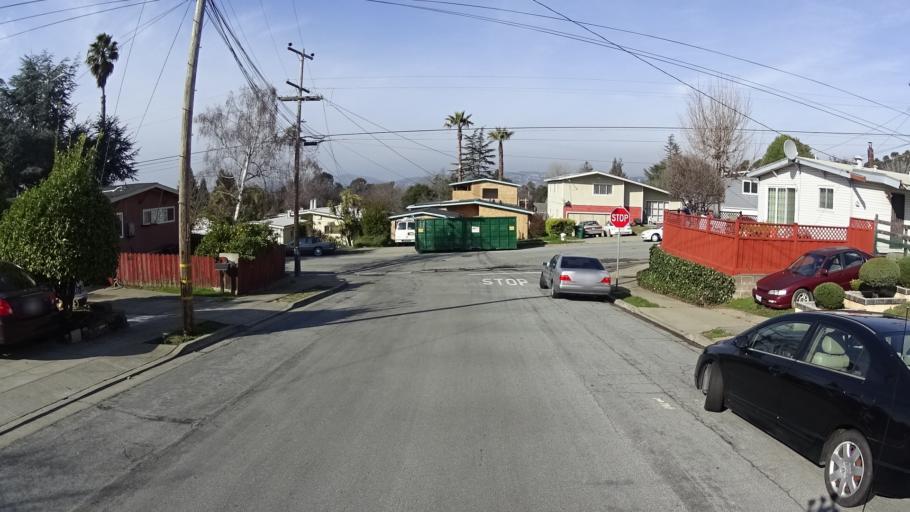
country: US
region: California
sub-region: Alameda County
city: Fairview
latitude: 37.6848
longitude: -122.0463
